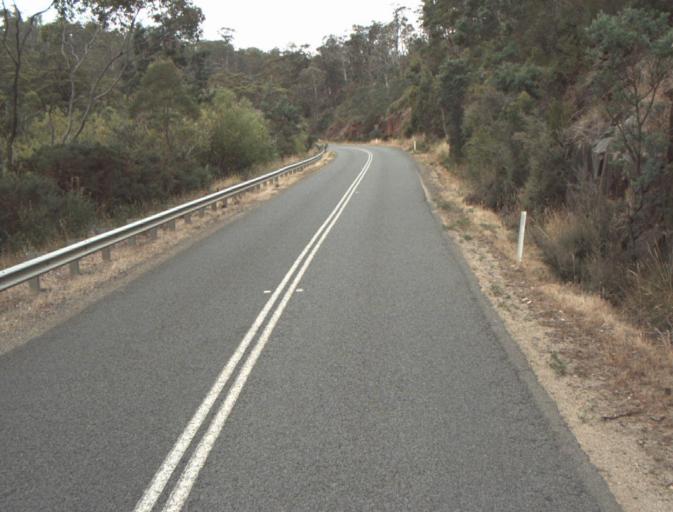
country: AU
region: Tasmania
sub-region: Northern Midlands
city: Evandale
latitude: -41.4946
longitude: 147.4238
